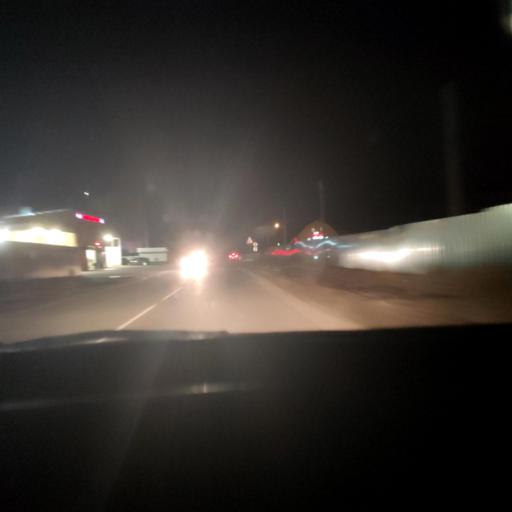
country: RU
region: Voronezj
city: Podgornoye
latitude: 51.7211
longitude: 39.1475
